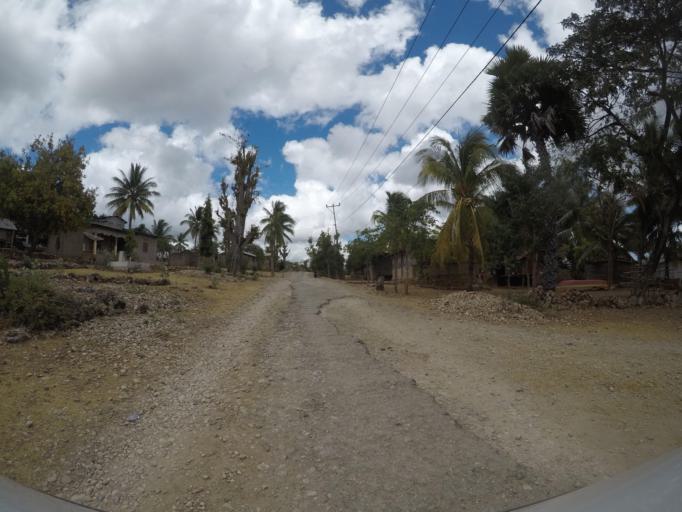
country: TL
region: Lautem
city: Lospalos
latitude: -8.3821
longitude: 126.9208
